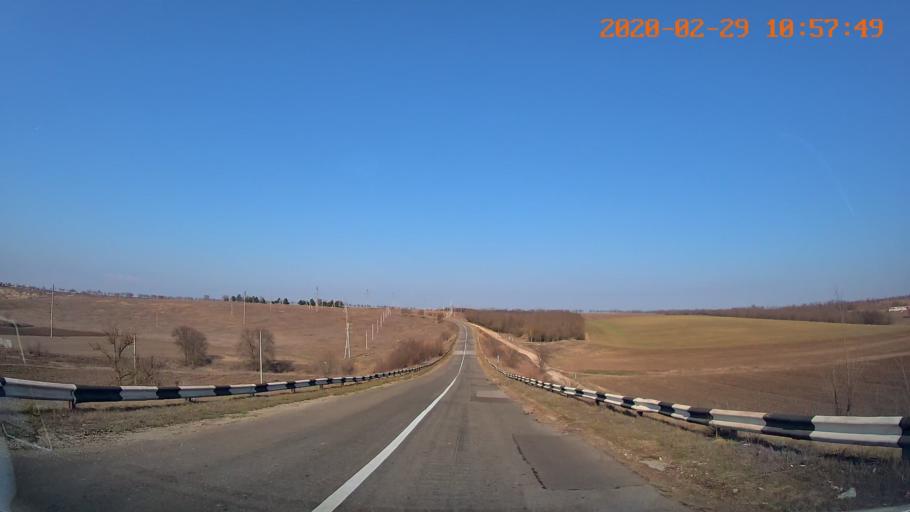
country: MD
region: Telenesti
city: Grigoriopol
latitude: 47.1636
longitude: 29.3202
